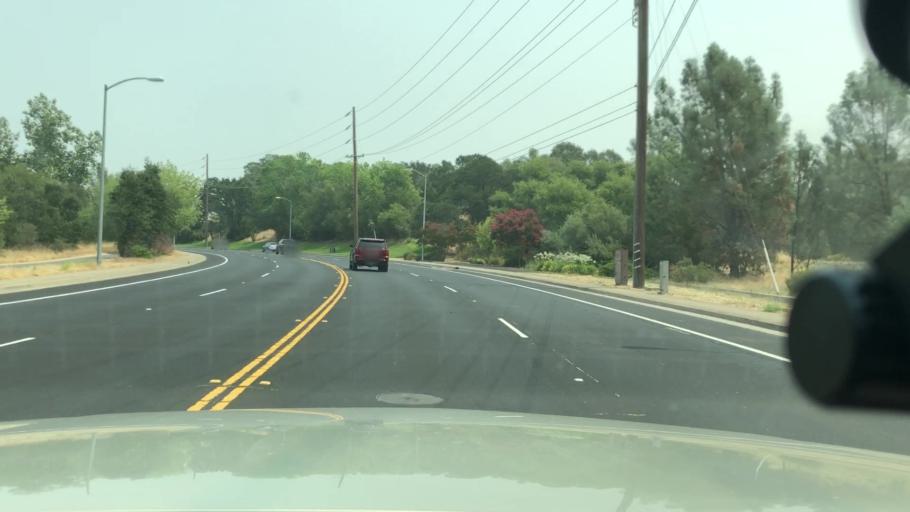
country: US
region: California
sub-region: Sacramento County
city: Folsom
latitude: 38.6581
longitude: -121.1615
